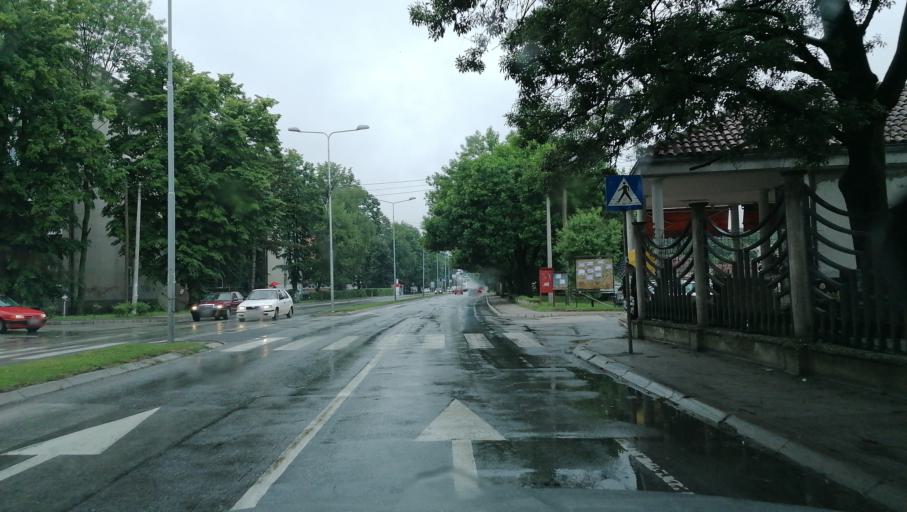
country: RS
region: Central Serbia
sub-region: Raski Okrug
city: Kraljevo
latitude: 43.7283
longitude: 20.6845
